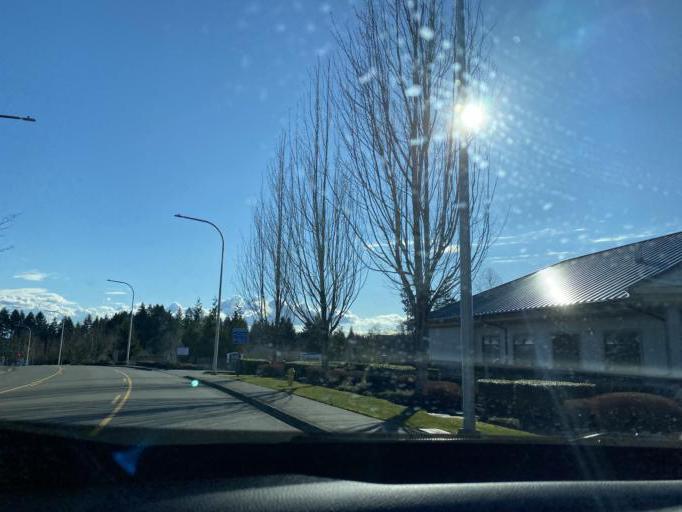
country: US
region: Washington
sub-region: King County
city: Federal Way
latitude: 47.3025
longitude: -122.3227
